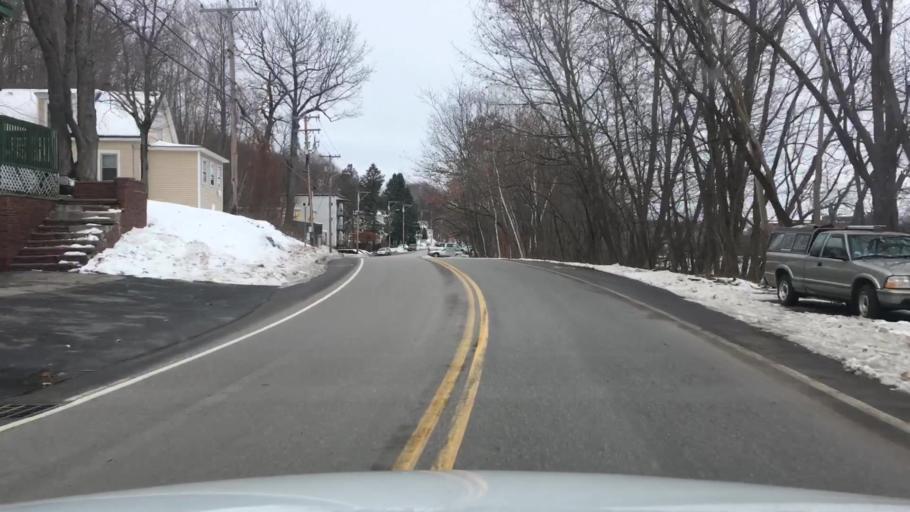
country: US
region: Maine
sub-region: Androscoggin County
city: Lewiston
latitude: 44.0842
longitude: -70.2150
